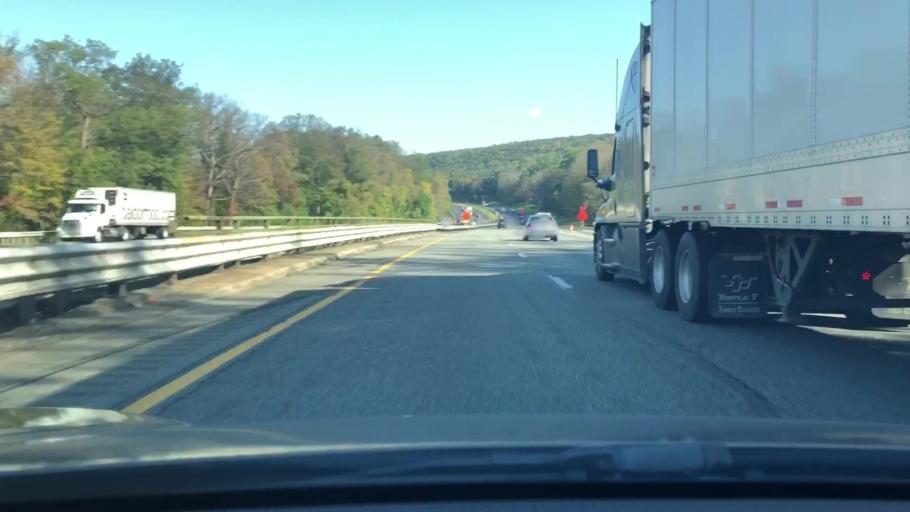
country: US
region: New York
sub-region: Rockland County
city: Sloatsburg
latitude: 41.2278
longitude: -74.1815
